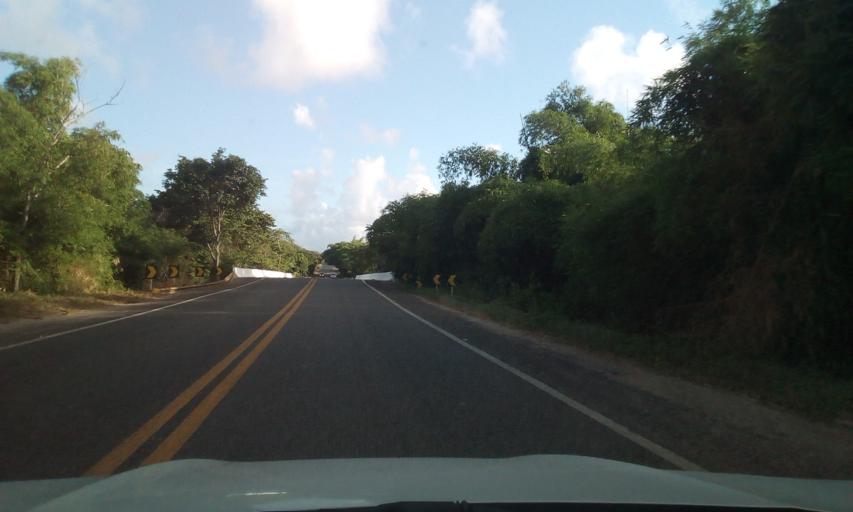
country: BR
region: Bahia
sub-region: Mata De Sao Joao
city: Mata de Sao Joao
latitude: -12.3842
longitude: -37.9129
